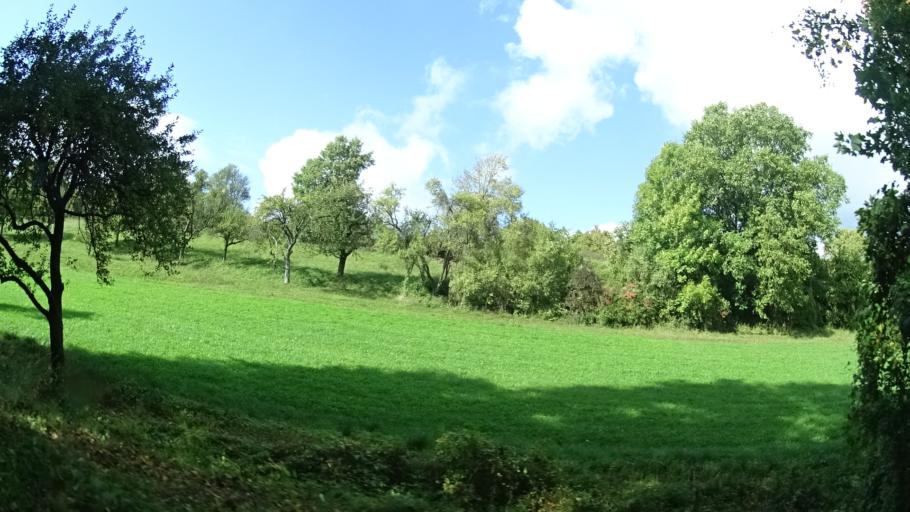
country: DE
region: Bavaria
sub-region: Regierungsbezirk Unterfranken
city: Neubrunn
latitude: 49.6839
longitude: 9.7000
